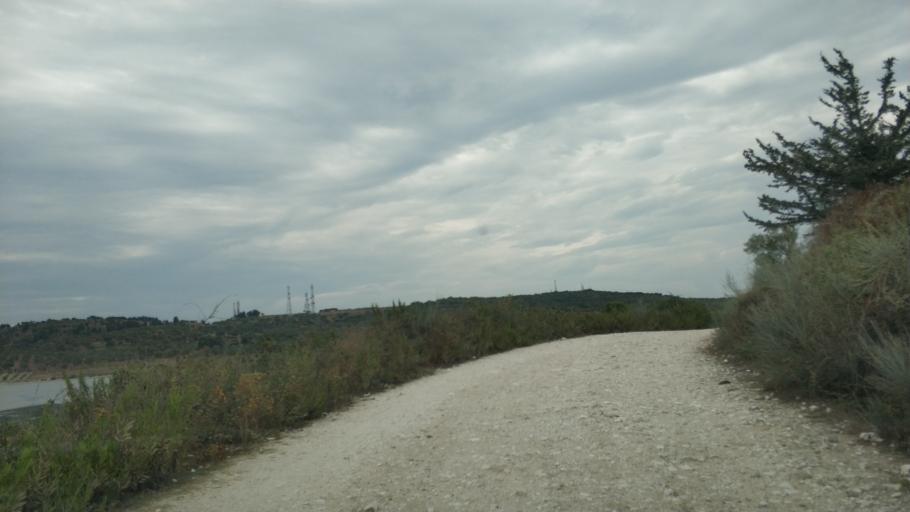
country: AL
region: Vlore
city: Vlore
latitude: 40.5116
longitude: 19.4020
